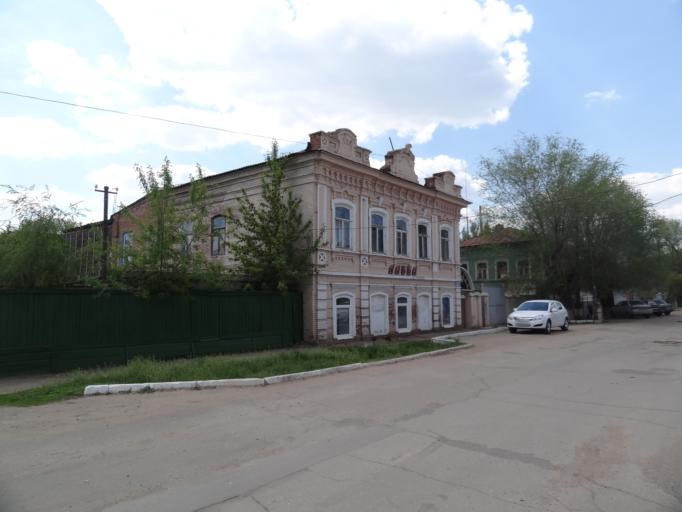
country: RU
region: Saratov
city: Engel's
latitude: 51.4995
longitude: 46.1334
